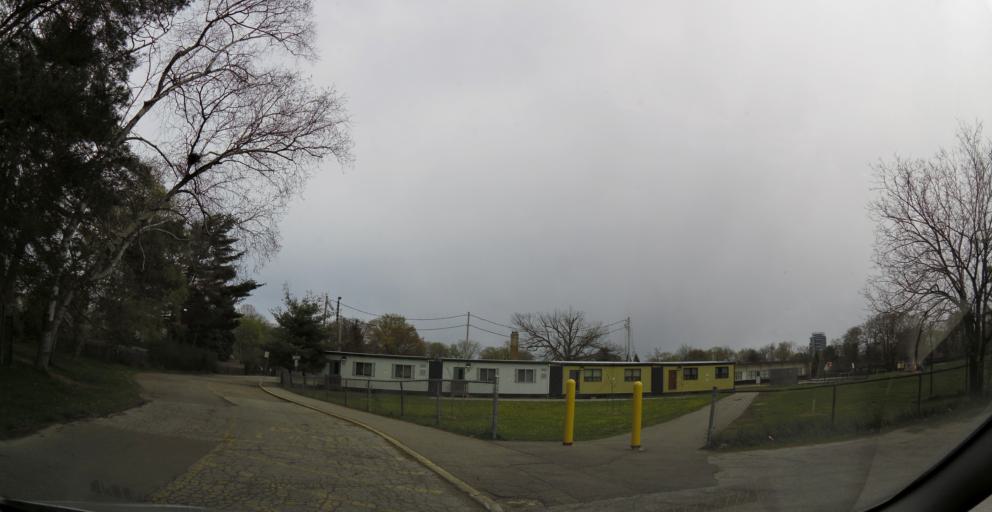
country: CA
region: Ontario
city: Mississauga
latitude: 43.5639
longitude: -79.5862
